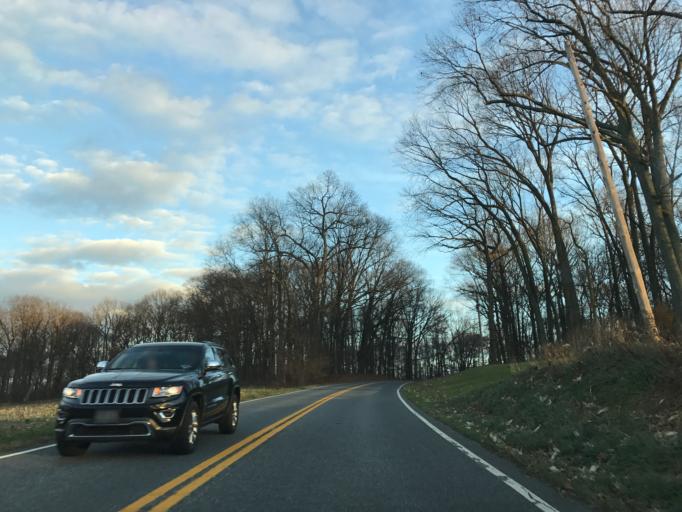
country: US
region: Pennsylvania
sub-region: York County
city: Susquehanna Trails
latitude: 39.7159
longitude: -76.2743
